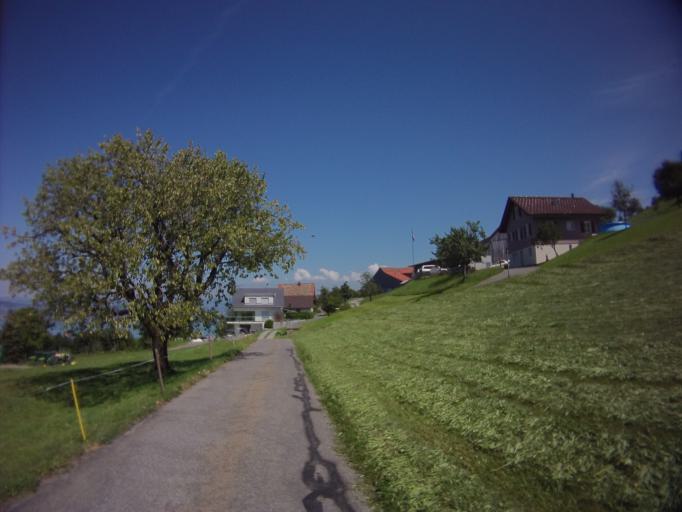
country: CH
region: Schwyz
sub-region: Bezirk Hoefe
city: Feusisberg
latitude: 47.1801
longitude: 8.7381
